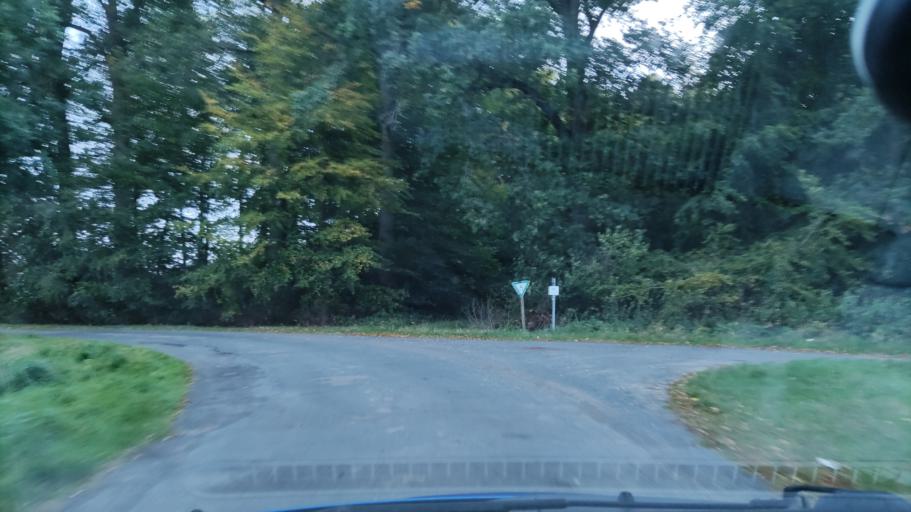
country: DE
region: Lower Saxony
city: Tosterglope
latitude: 53.2231
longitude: 10.8266
